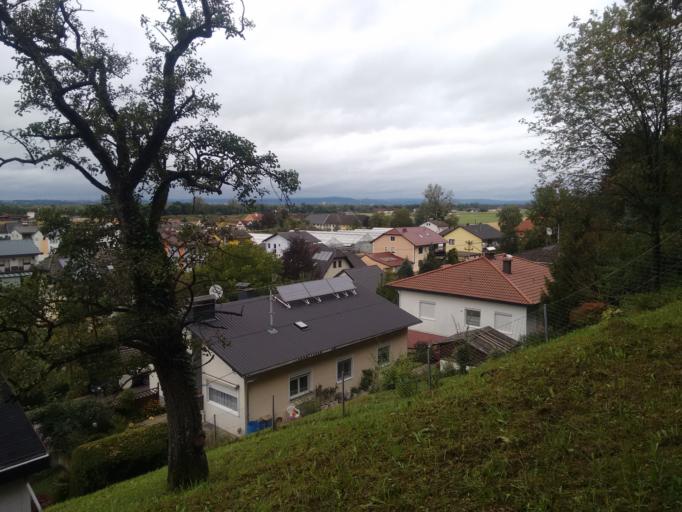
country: AT
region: Upper Austria
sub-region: Wels-Land
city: Marchtrenk
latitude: 48.1679
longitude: 14.1424
